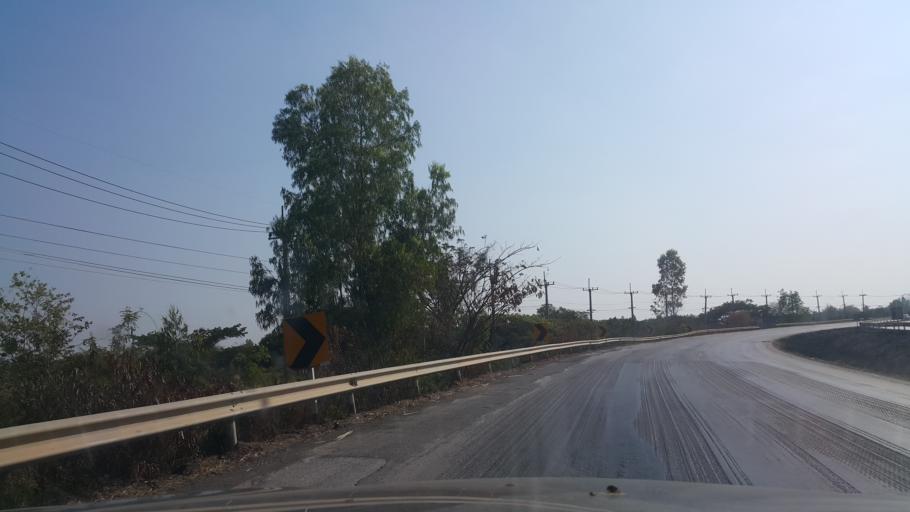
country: TH
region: Khon Kaen
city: Khon Kaen
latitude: 16.4206
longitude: 102.9169
